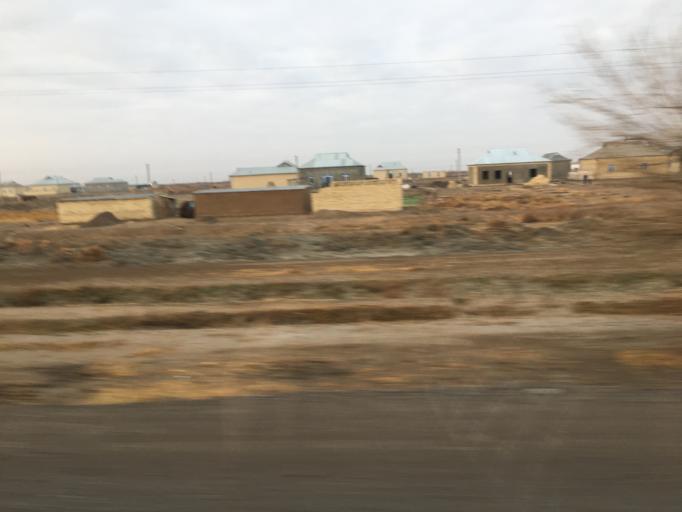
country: TM
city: Murgab
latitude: 37.4817
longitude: 62.0021
